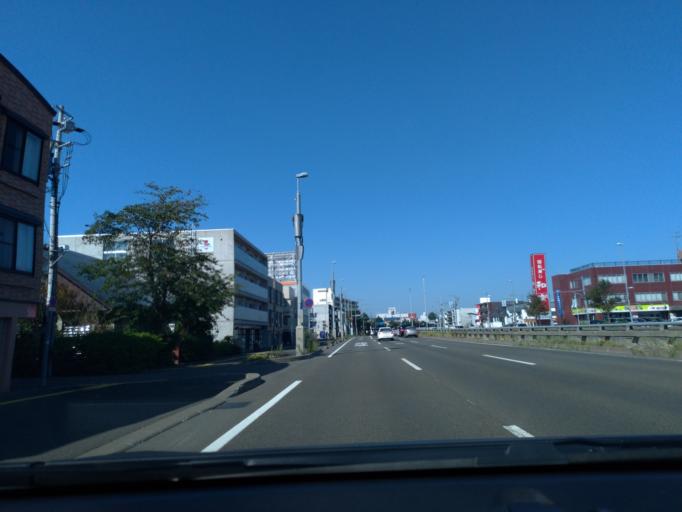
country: JP
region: Hokkaido
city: Sapporo
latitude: 43.1087
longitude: 141.3437
